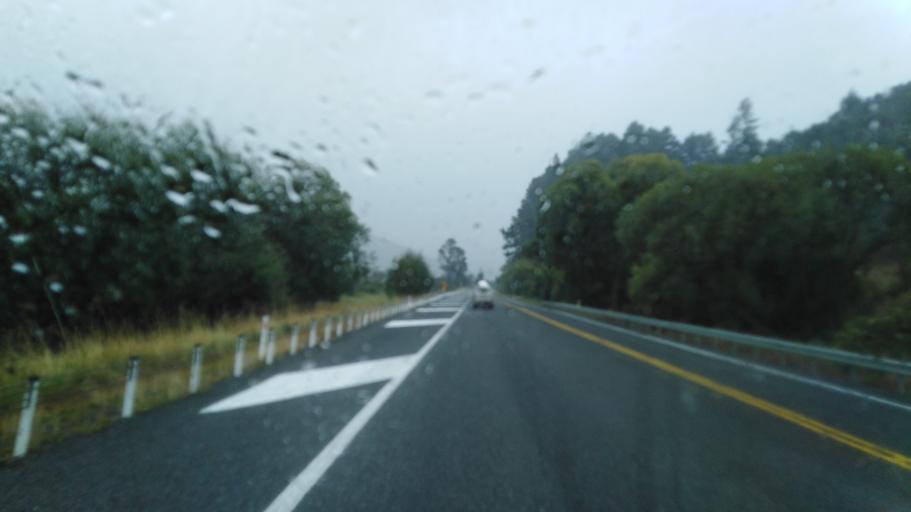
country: NZ
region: Marlborough
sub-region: Marlborough District
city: Picton
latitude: -41.3773
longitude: 173.9468
